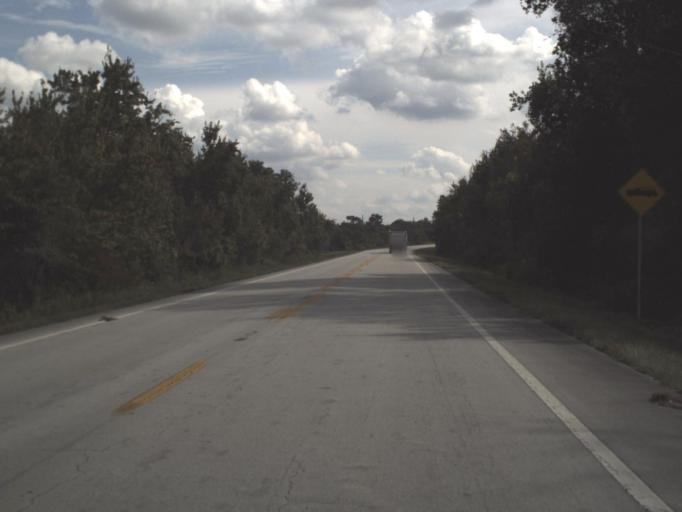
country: US
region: Florida
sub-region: Okeechobee County
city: Cypress Quarters
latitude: 27.5355
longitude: -80.8092
